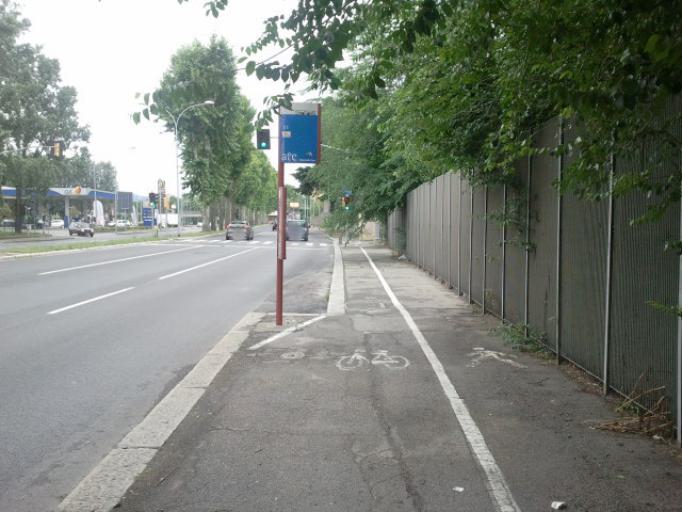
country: IT
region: Emilia-Romagna
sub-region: Provincia di Bologna
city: Bologna
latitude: 44.5211
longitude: 11.3624
